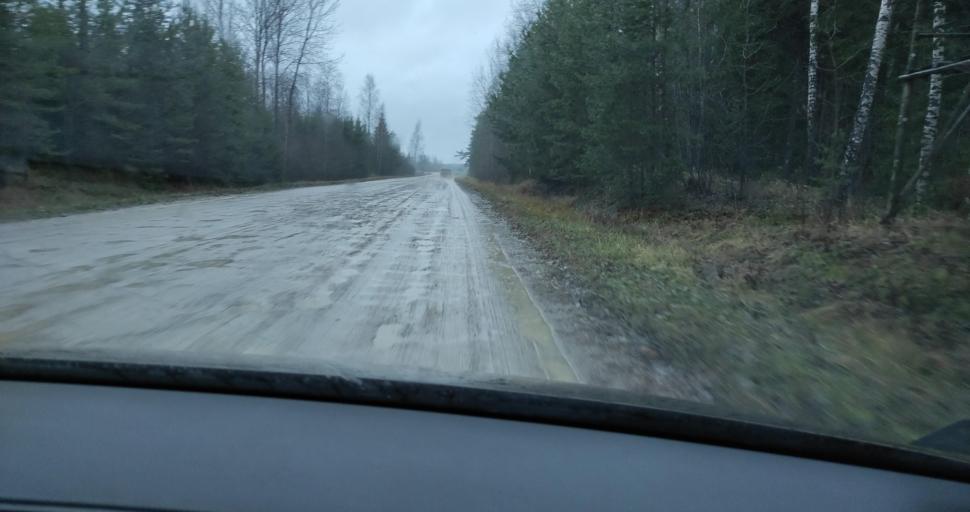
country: LV
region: Skrunda
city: Skrunda
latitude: 56.5960
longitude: 22.1140
